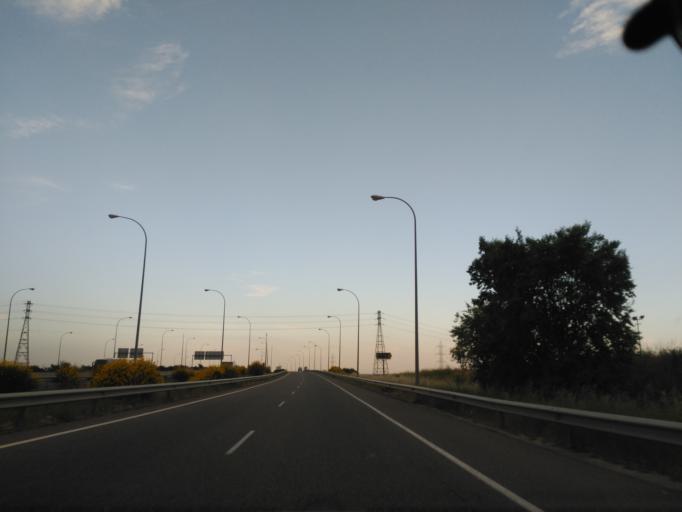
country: ES
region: Madrid
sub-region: Provincia de Madrid
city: Villaverde
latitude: 40.3262
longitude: -3.7115
